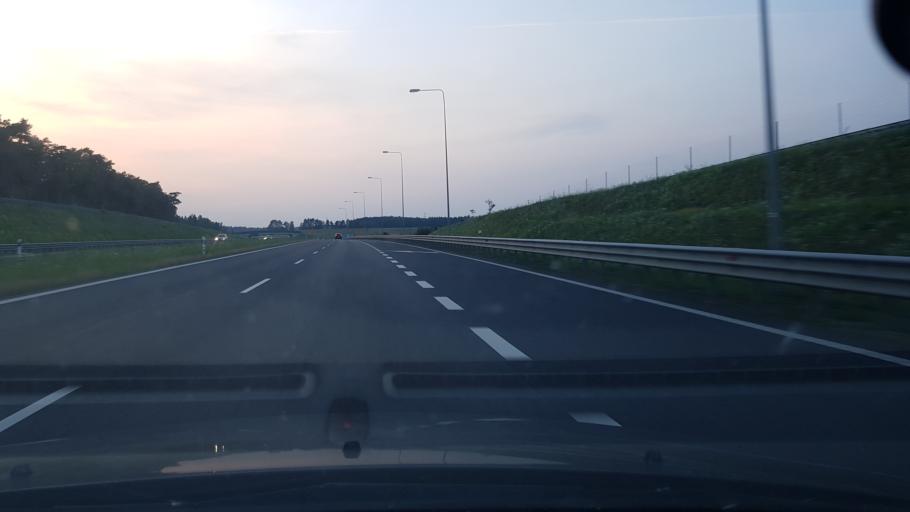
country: PL
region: Warmian-Masurian Voivodeship
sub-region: Powiat olsztynski
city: Olsztynek
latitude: 53.5039
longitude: 20.3100
